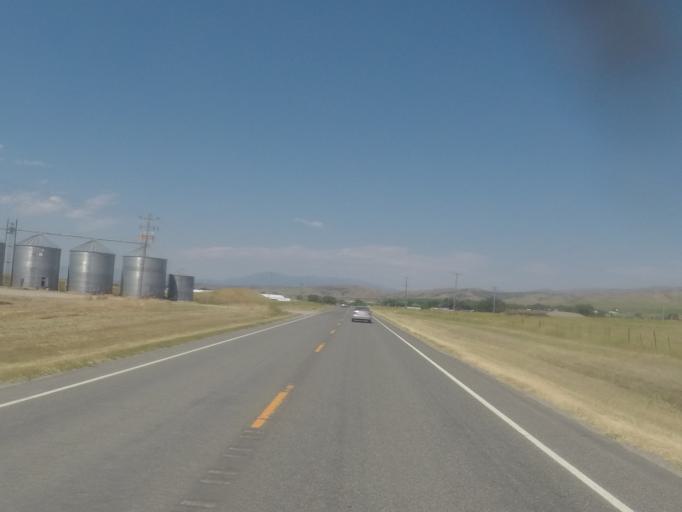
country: US
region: Montana
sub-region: Broadwater County
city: Townsend
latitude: 46.1652
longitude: -111.4530
